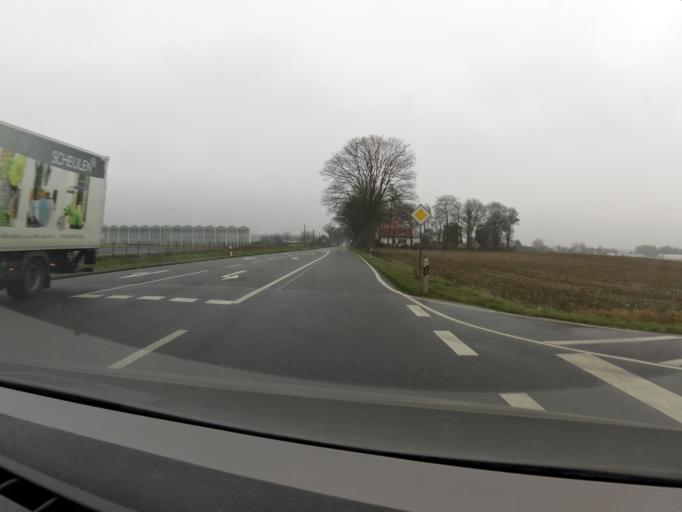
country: DE
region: North Rhine-Westphalia
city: Straelen
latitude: 51.4034
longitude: 6.2610
